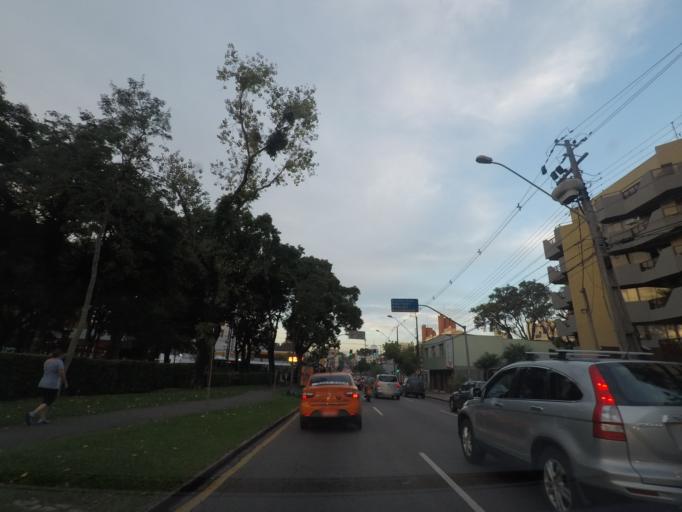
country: BR
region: Parana
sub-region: Curitiba
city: Curitiba
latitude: -25.4286
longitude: -49.2854
